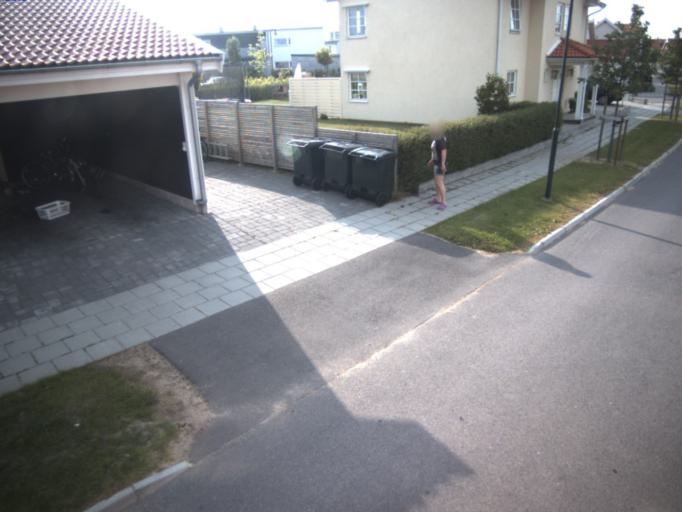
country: SE
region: Skane
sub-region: Helsingborg
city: Odakra
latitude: 56.0835
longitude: 12.7021
